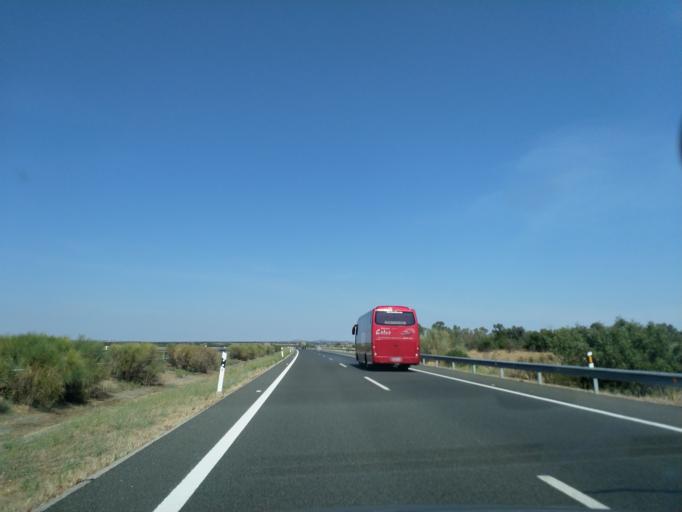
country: ES
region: Extremadura
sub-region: Provincia de Caceres
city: Casas de Don Antonio
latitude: 39.2472
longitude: -6.3065
